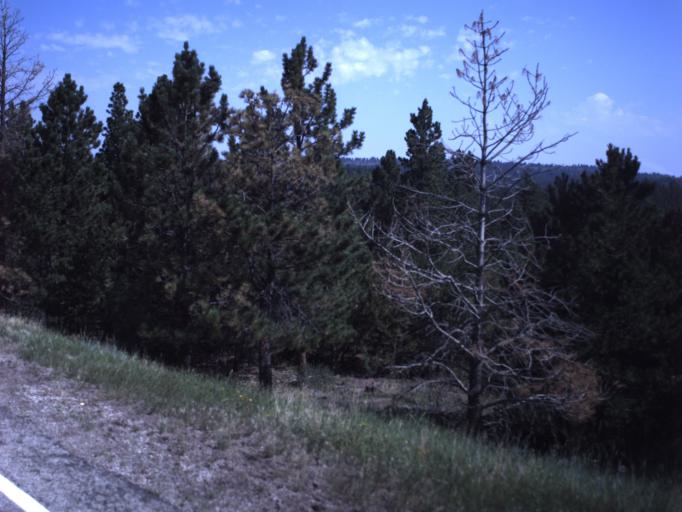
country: US
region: Utah
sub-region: Daggett County
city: Manila
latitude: 40.8487
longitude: -109.6695
